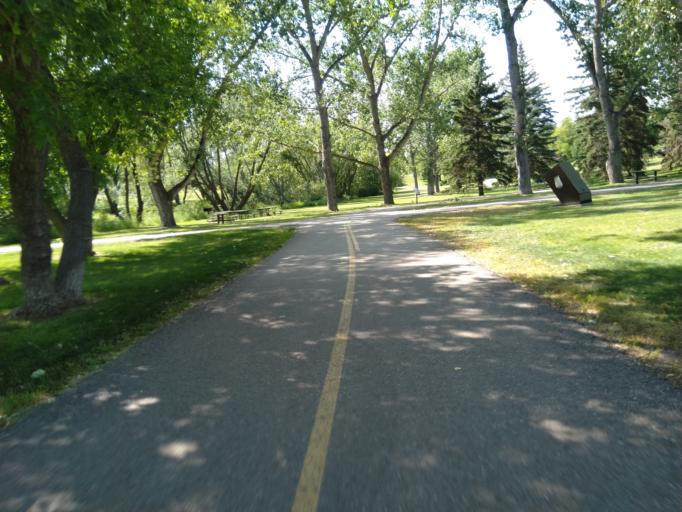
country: CA
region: Alberta
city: Calgary
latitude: 51.0740
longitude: -114.0919
